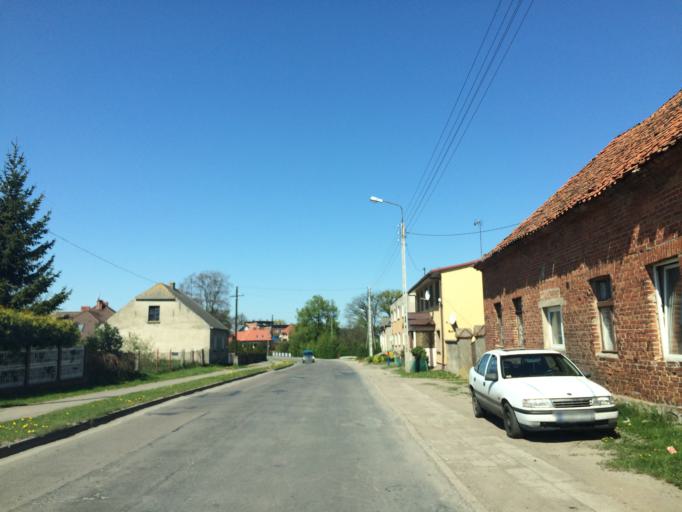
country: PL
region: Warmian-Masurian Voivodeship
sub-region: Powiat nowomiejski
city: Biskupiec
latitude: 53.5023
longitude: 19.3553
